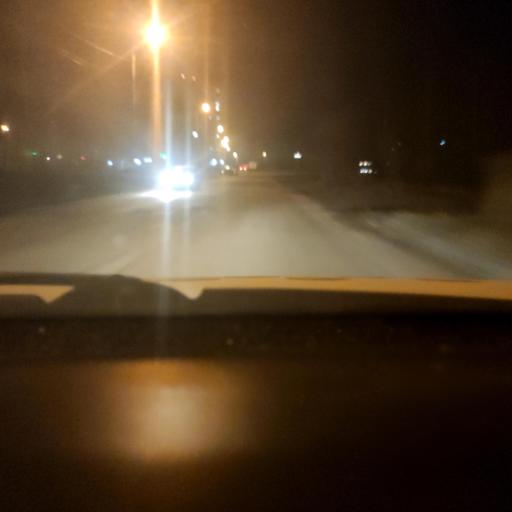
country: RU
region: Perm
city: Polazna
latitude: 58.1329
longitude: 56.3915
